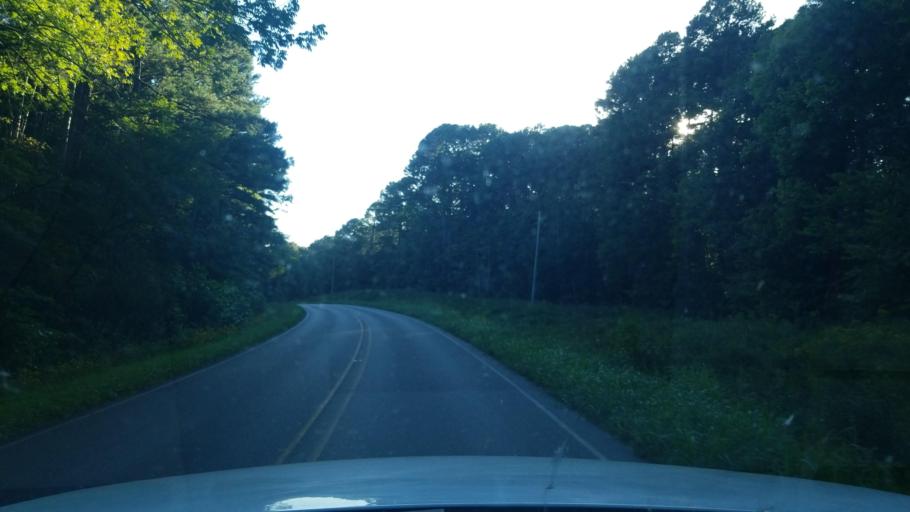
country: US
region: Illinois
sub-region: Hardin County
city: Elizabethtown
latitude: 37.5768
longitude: -88.3868
